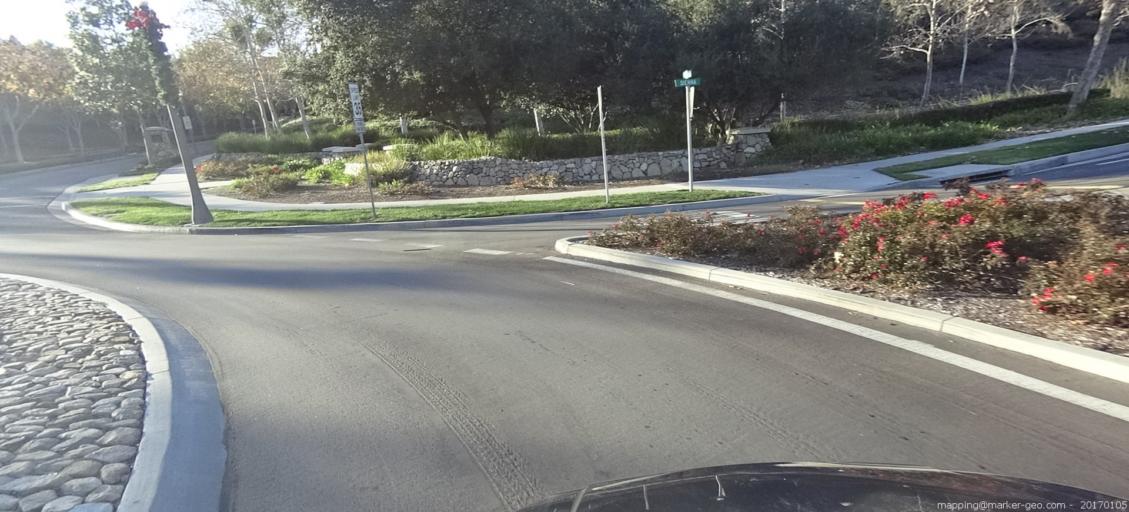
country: US
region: California
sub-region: Orange County
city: Ladera Ranch
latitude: 33.5522
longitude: -117.6384
